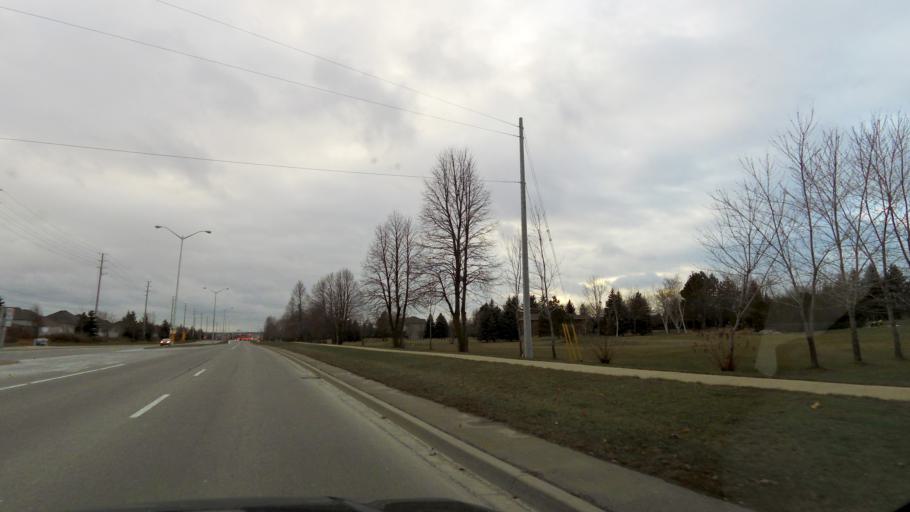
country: CA
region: Ontario
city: Brampton
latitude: 43.7762
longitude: -79.7077
